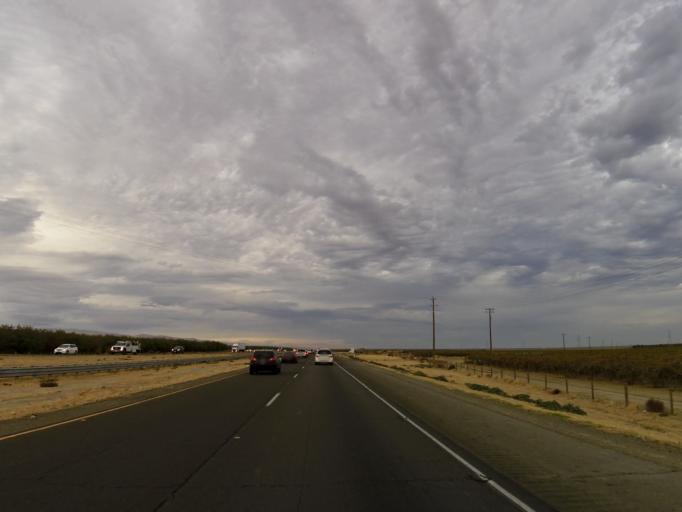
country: US
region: California
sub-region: Fresno County
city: Coalinga
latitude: 36.3726
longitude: -120.3375
